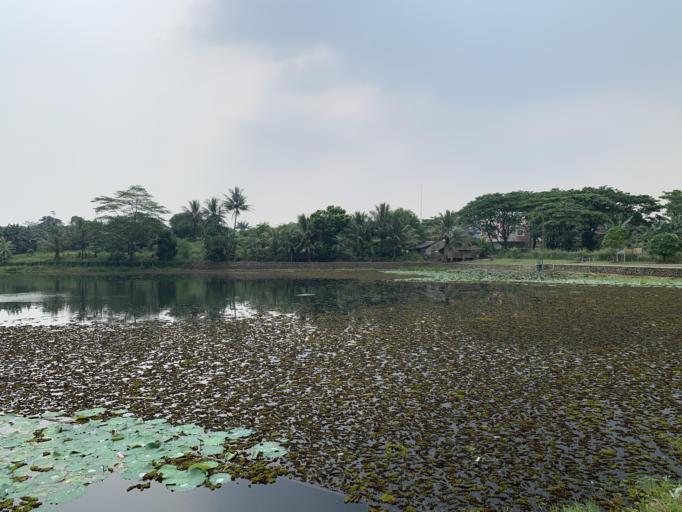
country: ID
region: West Java
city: Serpong
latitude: -6.3839
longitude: 106.6364
